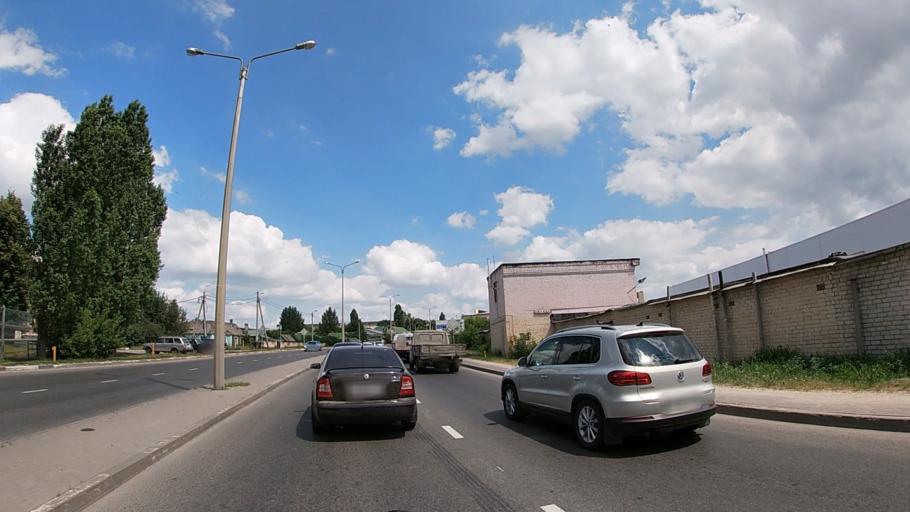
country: RU
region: Belgorod
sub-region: Belgorodskiy Rayon
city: Belgorod
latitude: 50.6110
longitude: 36.5341
